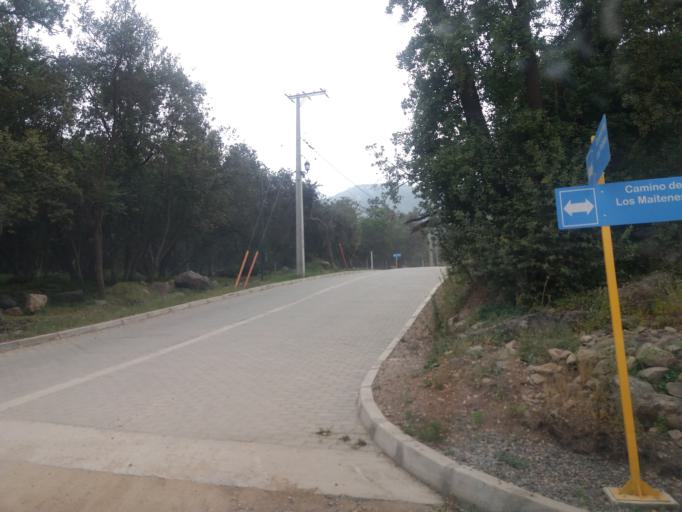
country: CL
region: Valparaiso
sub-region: Provincia de Marga Marga
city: Limache
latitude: -33.0248
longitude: -71.1290
